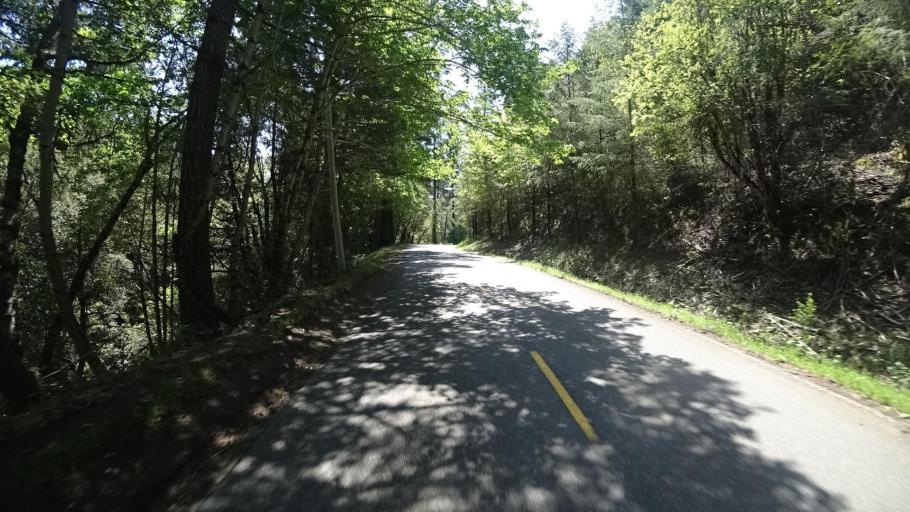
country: US
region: California
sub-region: Humboldt County
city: Redway
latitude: 40.1361
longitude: -123.6293
